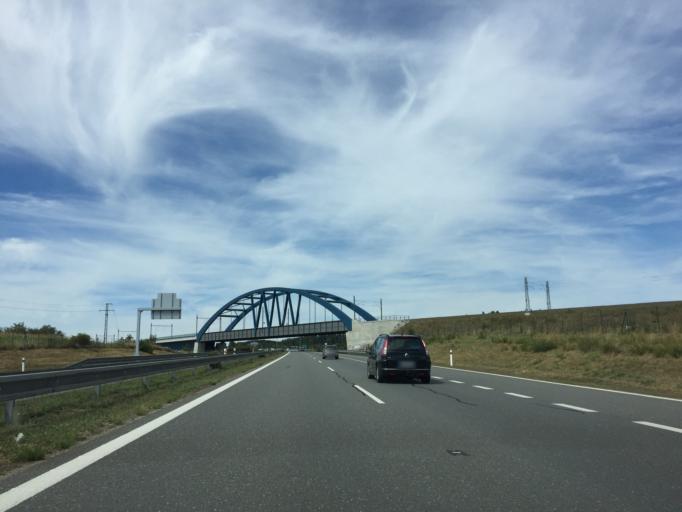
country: CZ
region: Jihocesky
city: Chotoviny
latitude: 49.4774
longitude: 14.6603
